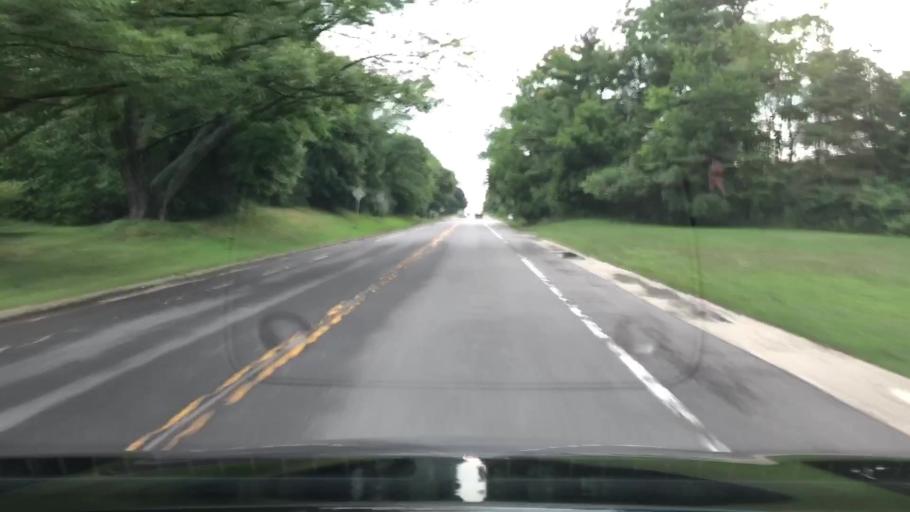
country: US
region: New York
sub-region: Erie County
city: Orchard Park
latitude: 42.7526
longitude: -78.7033
